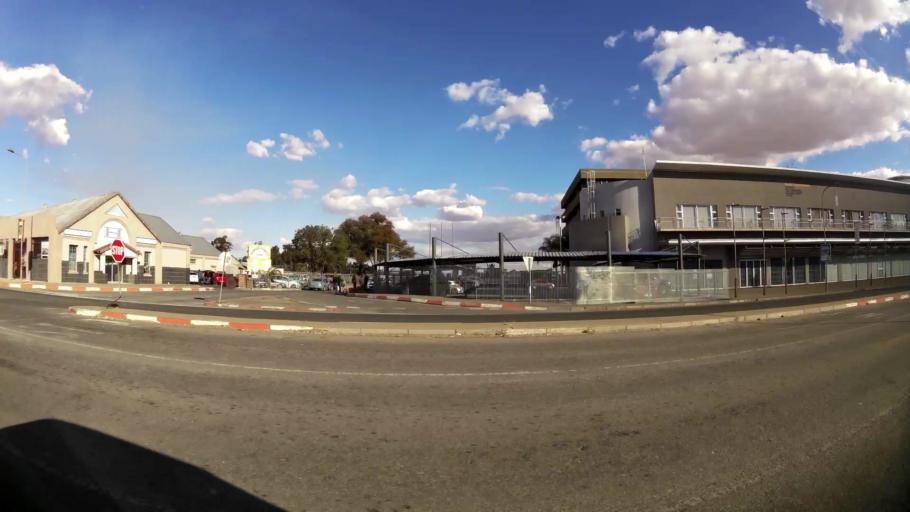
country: ZA
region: North-West
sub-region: Dr Kenneth Kaunda District Municipality
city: Klerksdorp
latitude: -26.8765
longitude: 26.6655
